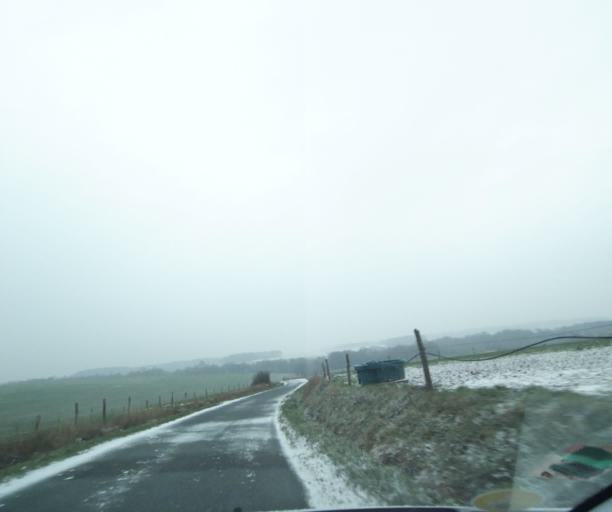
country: FR
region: Champagne-Ardenne
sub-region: Departement de la Haute-Marne
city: Wassy
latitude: 48.4780
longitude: 5.0391
